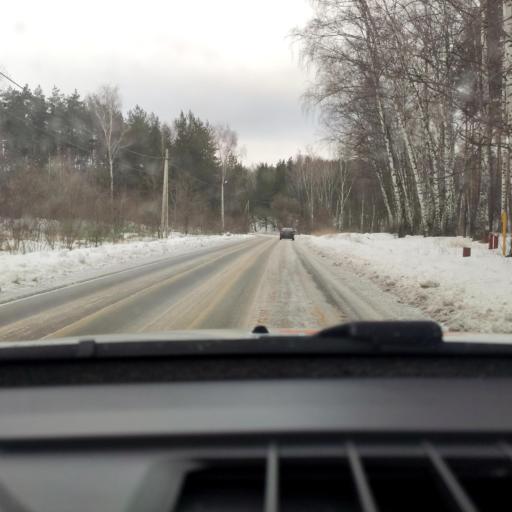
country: RU
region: Voronezj
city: Podgornoye
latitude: 51.7501
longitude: 39.1577
